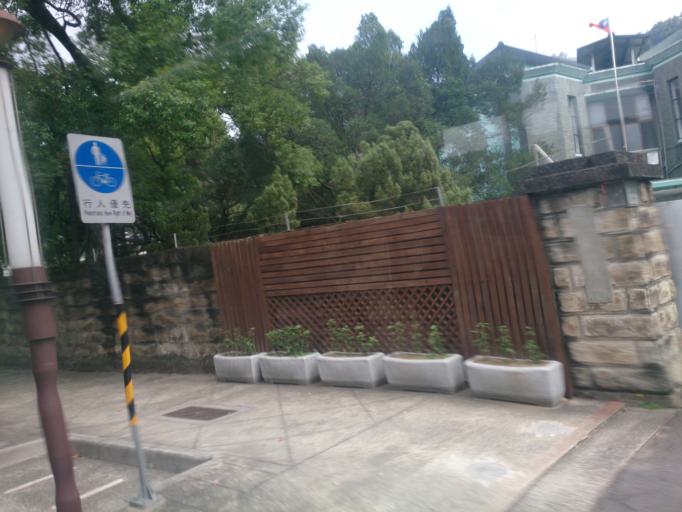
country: TW
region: Taipei
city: Taipei
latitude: 25.0885
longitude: 121.5275
